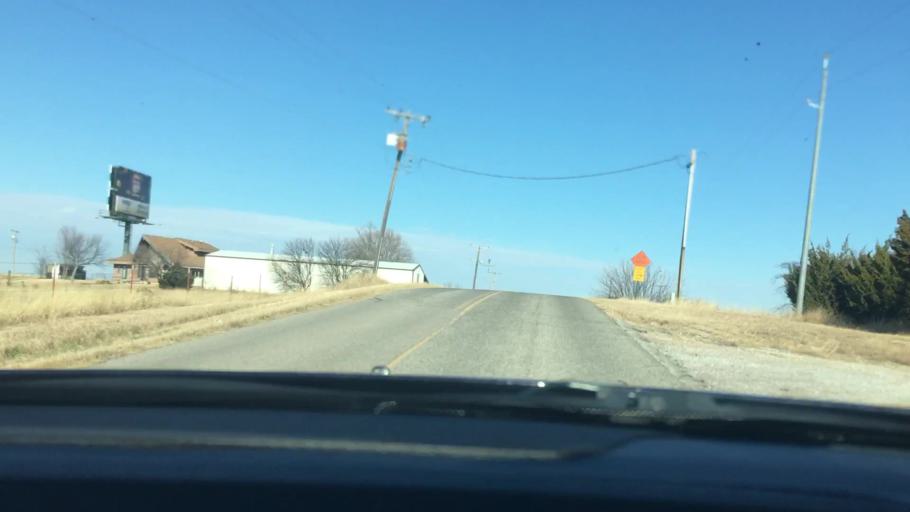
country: US
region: Oklahoma
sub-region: Murray County
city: Davis
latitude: 34.5043
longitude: -97.0553
